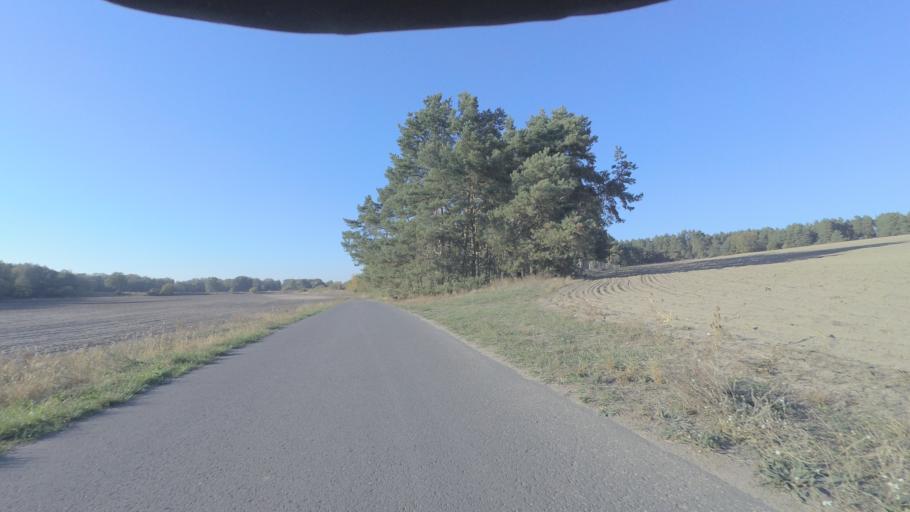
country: DE
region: Brandenburg
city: Mittenwalde
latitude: 52.2542
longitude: 13.5448
